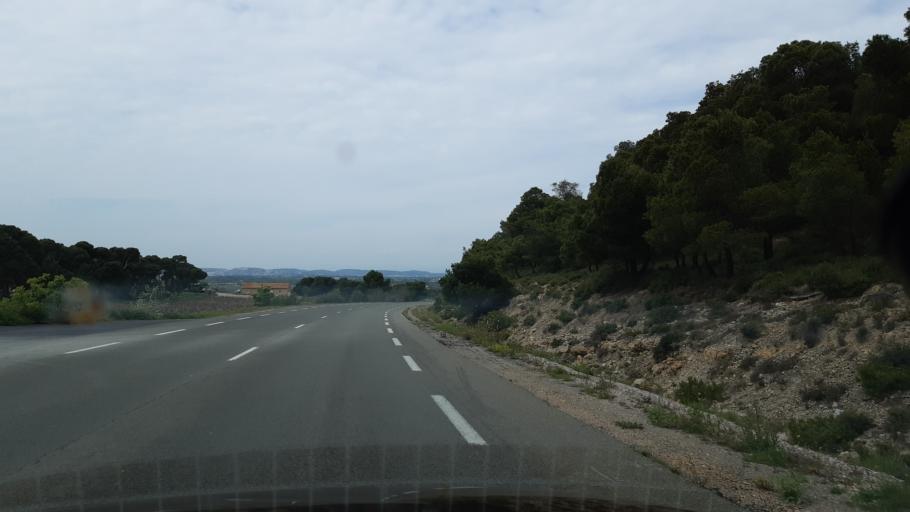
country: FR
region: Languedoc-Roussillon
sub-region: Departement de l'Aude
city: Gruissan
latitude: 43.1278
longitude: 3.0595
